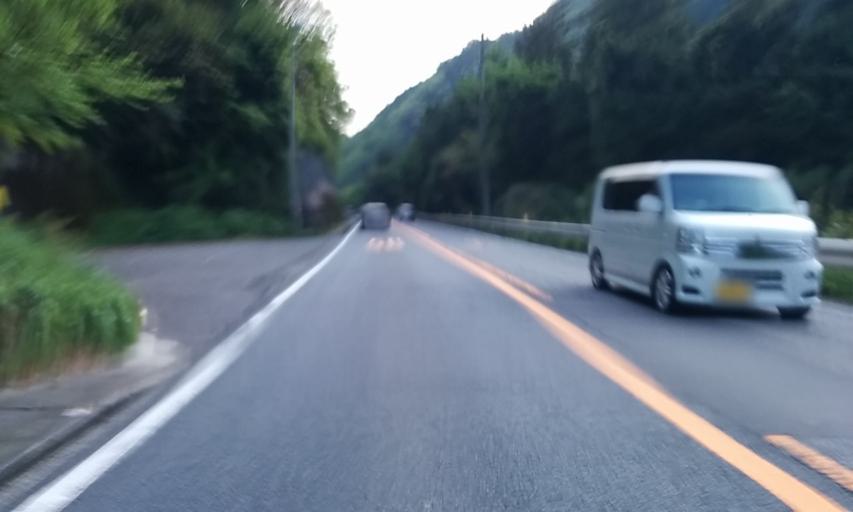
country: JP
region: Ehime
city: Saijo
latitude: 33.8432
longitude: 132.9948
